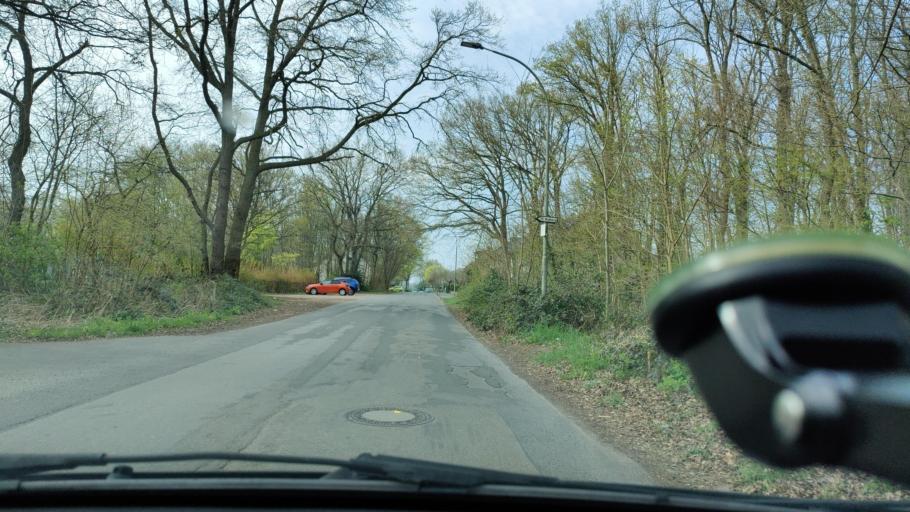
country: DE
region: North Rhine-Westphalia
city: Rheinberg
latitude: 51.5274
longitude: 6.6388
